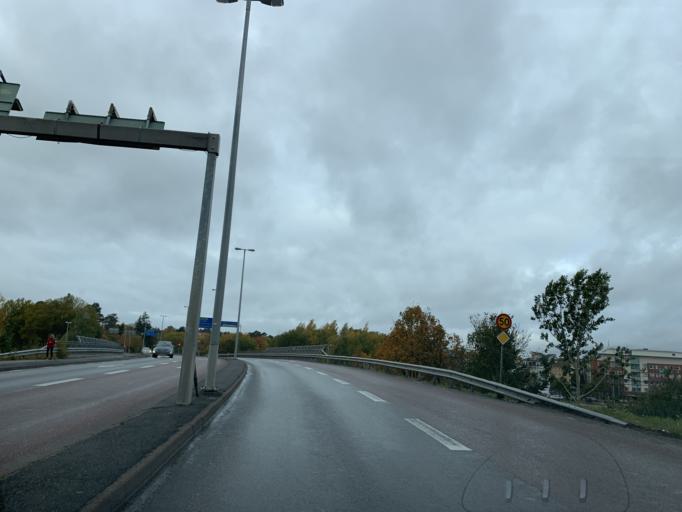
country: SE
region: Stockholm
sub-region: Huddinge Kommun
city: Huddinge
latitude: 59.2344
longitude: 17.9773
